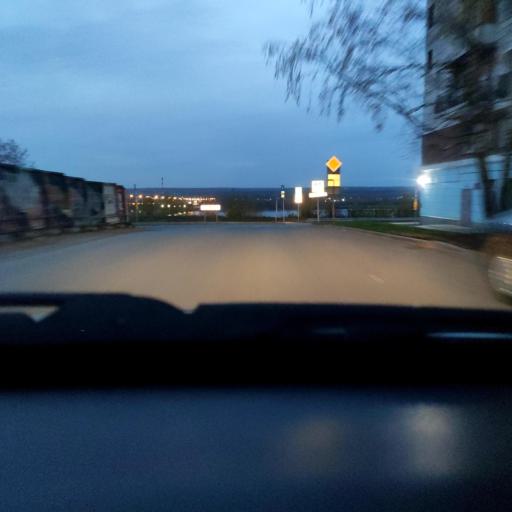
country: RU
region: Perm
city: Perm
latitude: 58.0152
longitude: 56.2273
